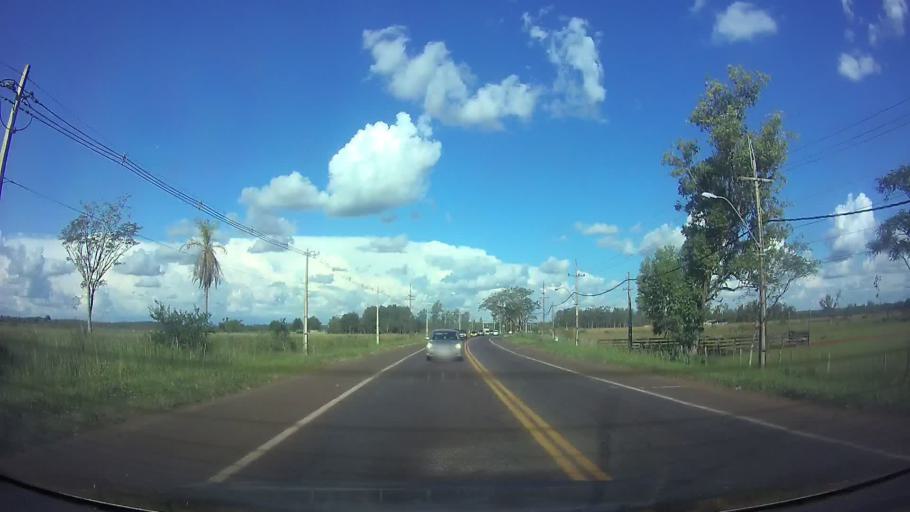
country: PY
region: Cordillera
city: Eusebio Ayala
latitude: -25.3803
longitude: -56.9885
